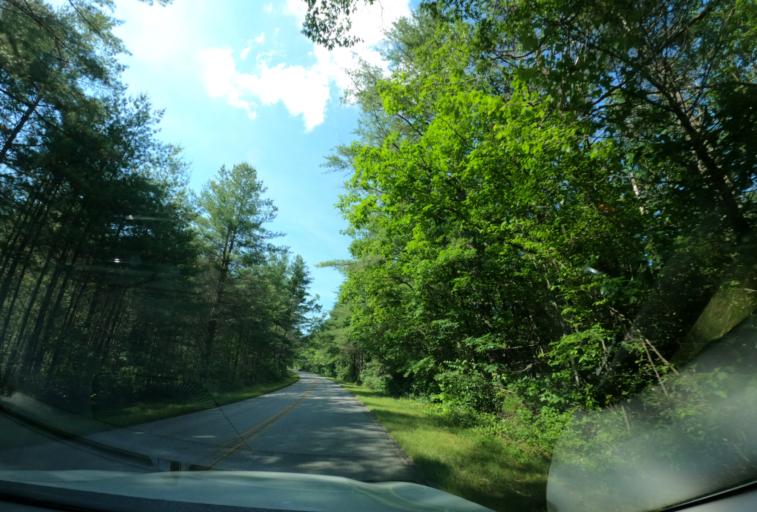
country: US
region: North Carolina
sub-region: Transylvania County
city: Brevard
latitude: 35.1751
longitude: -82.6389
